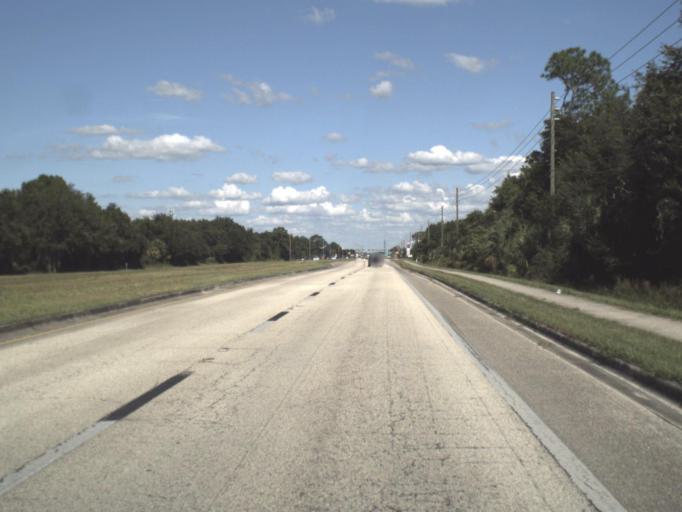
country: US
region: Florida
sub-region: Charlotte County
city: Port Charlotte
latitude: 27.0075
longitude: -82.1614
